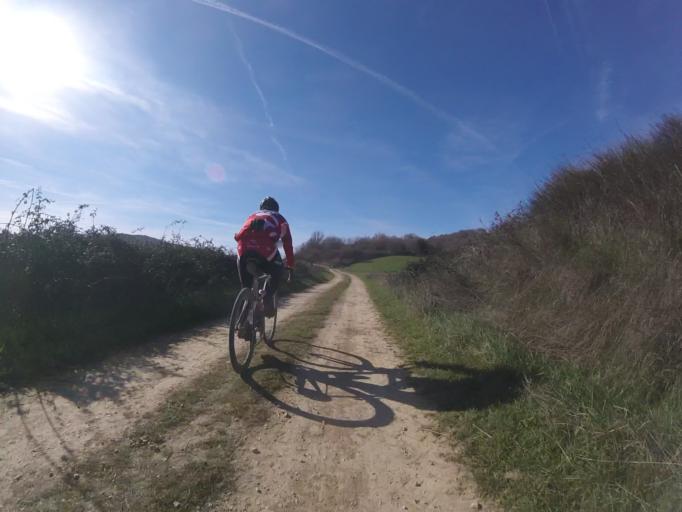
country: ES
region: Navarre
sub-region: Provincia de Navarra
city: Yerri
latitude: 42.6746
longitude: -1.9575
